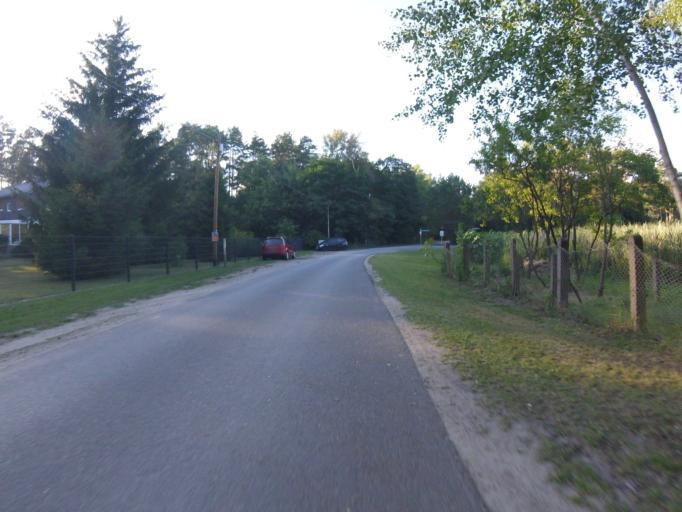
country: DE
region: Brandenburg
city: Gross Koris
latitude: 52.1773
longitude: 13.6552
